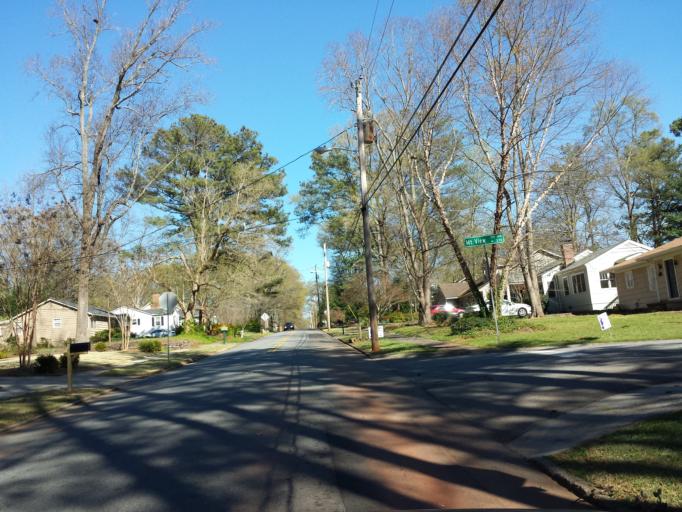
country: US
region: Georgia
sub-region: Cobb County
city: Marietta
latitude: 33.9593
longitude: -84.5634
